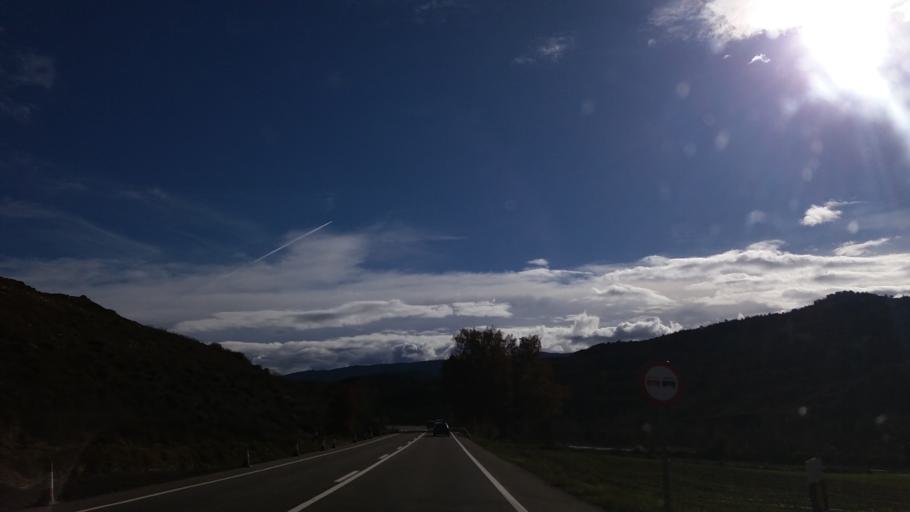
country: ES
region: Aragon
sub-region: Provincia de Huesca
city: Arguis
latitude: 42.4107
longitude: -0.3919
